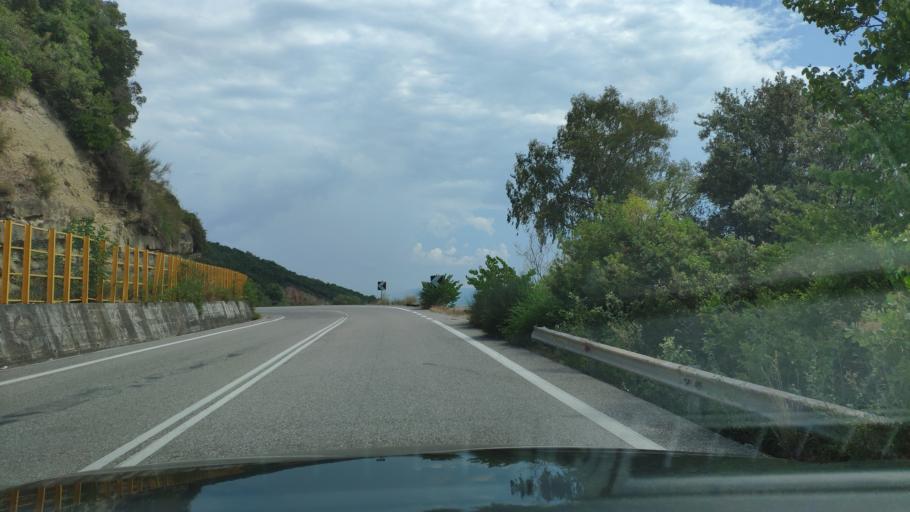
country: GR
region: West Greece
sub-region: Nomos Aitolias kai Akarnanias
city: Menidi
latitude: 39.0130
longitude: 21.1411
